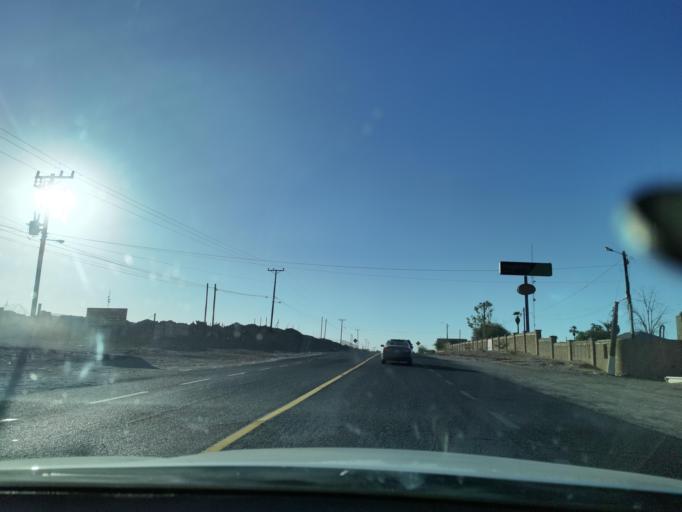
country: MX
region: Baja California
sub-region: Mexicali
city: Islas Agrarias Grupo A
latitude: 32.6404
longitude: -115.2994
